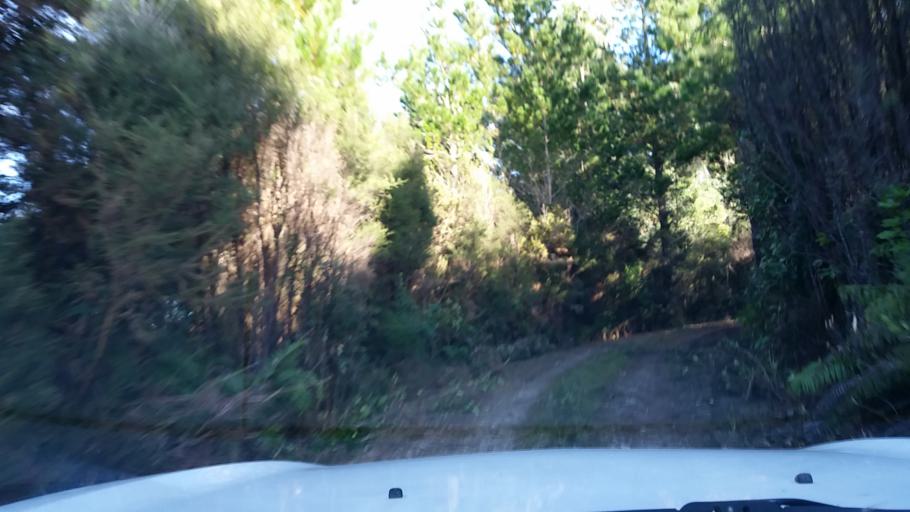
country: NZ
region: Waikato
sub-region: Otorohanga District
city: Otorohanga
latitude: -38.3071
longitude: 174.9561
